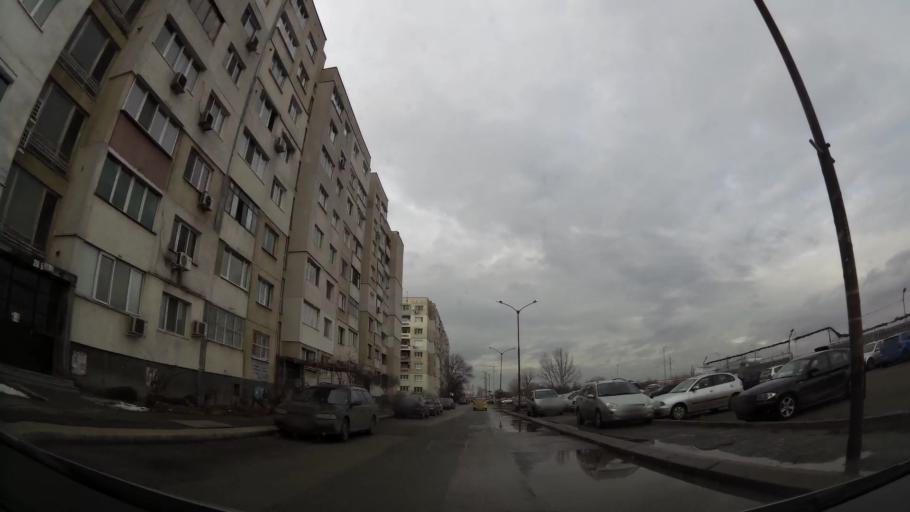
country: BG
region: Sofia-Capital
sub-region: Stolichna Obshtina
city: Sofia
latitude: 42.7460
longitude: 23.2805
